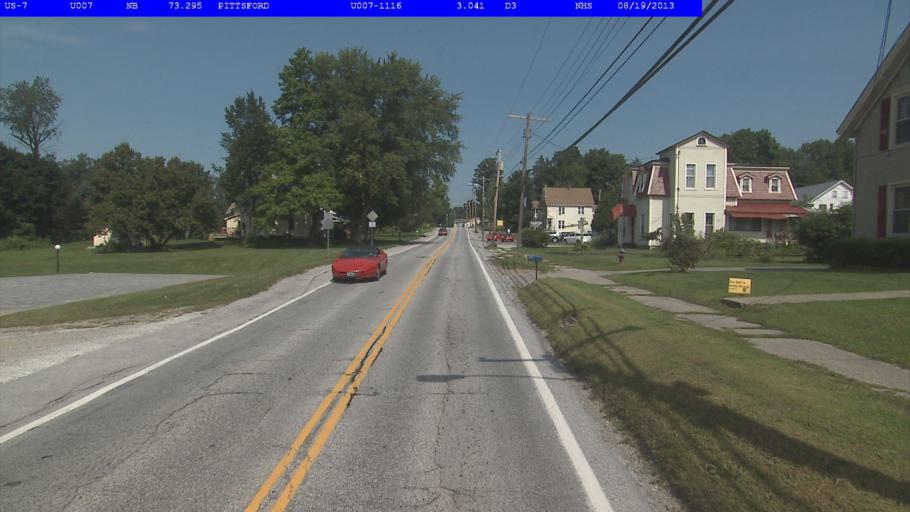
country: US
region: Vermont
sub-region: Rutland County
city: Rutland
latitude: 43.7029
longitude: -73.0124
